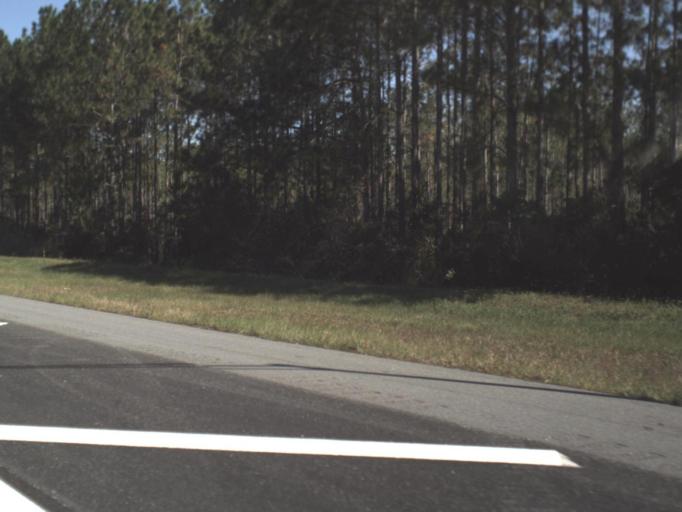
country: US
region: Florida
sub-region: Pasco County
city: Odessa
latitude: 28.2631
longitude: -82.5502
